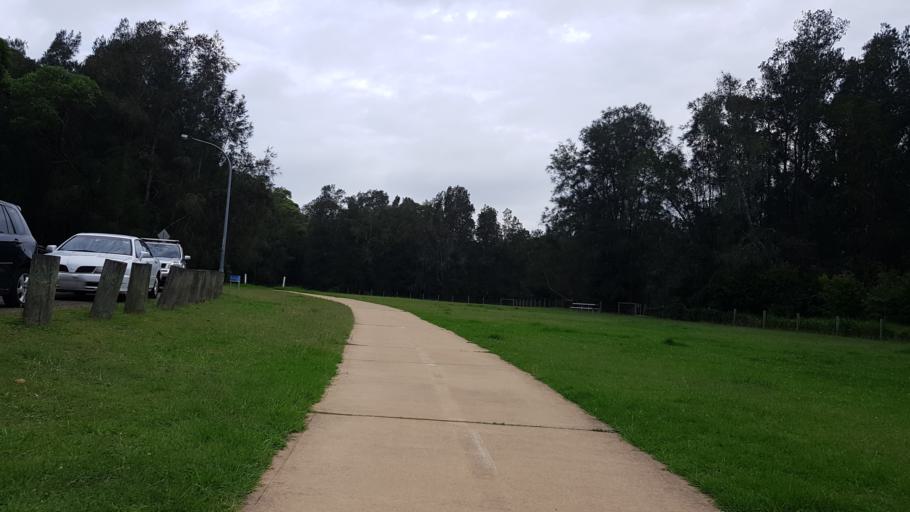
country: AU
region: New South Wales
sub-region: Warringah
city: Narrabeen
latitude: -33.7246
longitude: 151.2759
